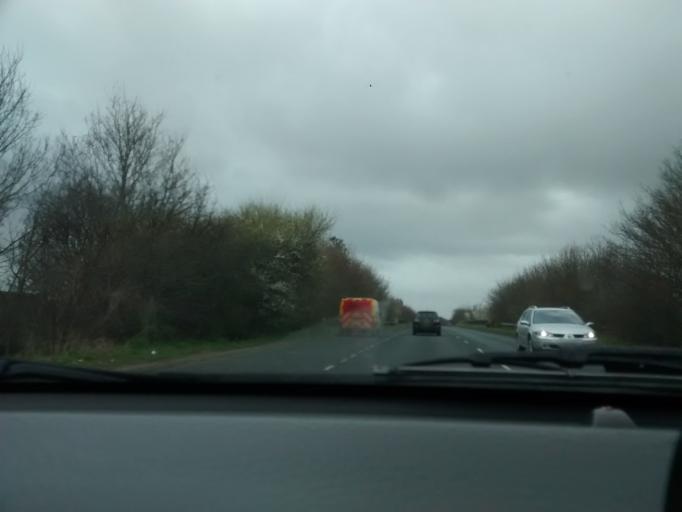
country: GB
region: England
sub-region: Suffolk
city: Felixstowe
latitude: 51.9742
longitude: 1.3424
